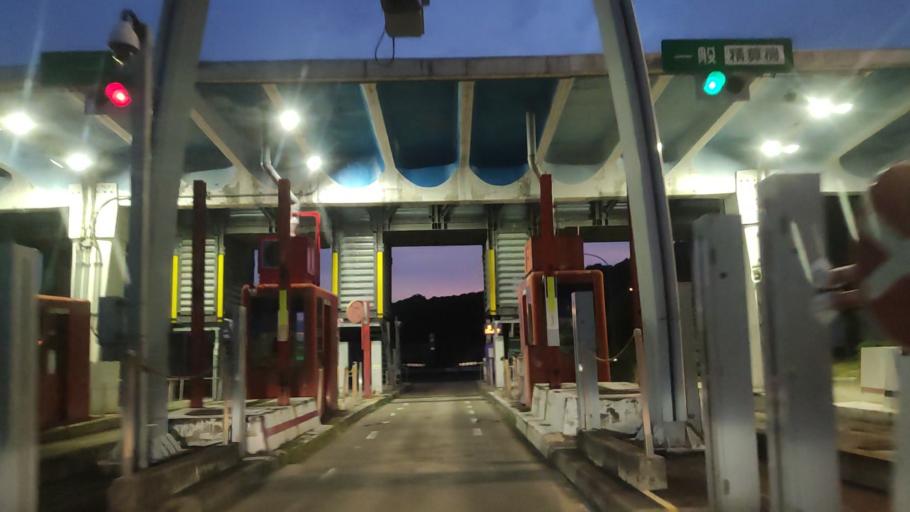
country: JP
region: Hyogo
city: Sandacho
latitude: 34.8869
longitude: 135.1154
